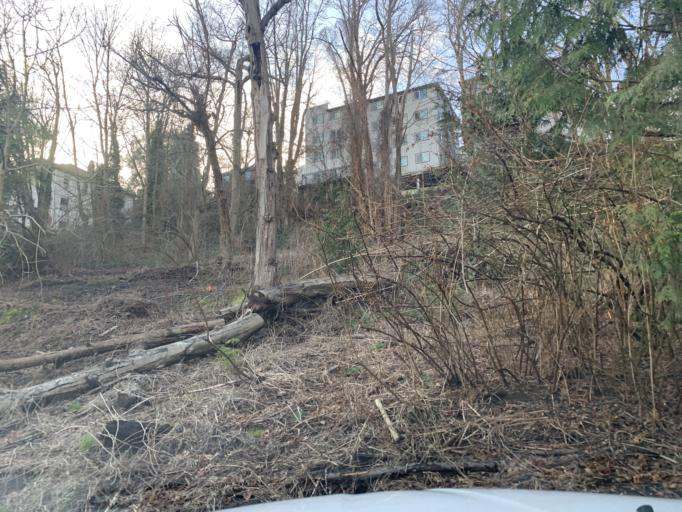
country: US
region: Washington
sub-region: King County
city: Seattle
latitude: 47.6625
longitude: -122.3028
